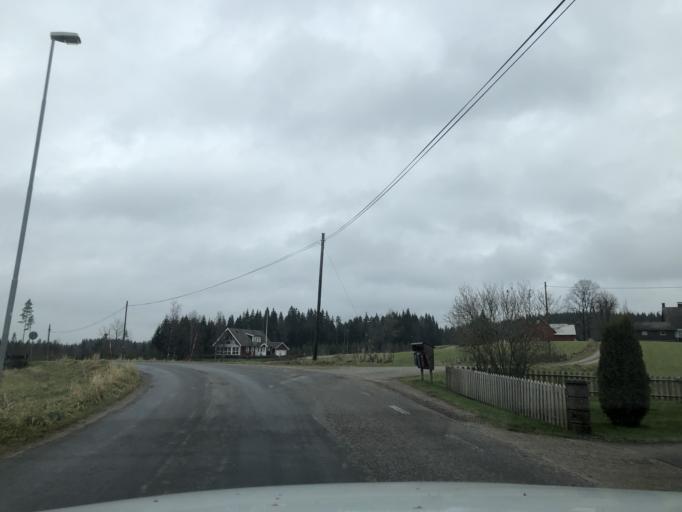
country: SE
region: Vaestra Goetaland
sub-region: Ulricehamns Kommun
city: Ulricehamn
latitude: 57.8642
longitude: 13.5545
